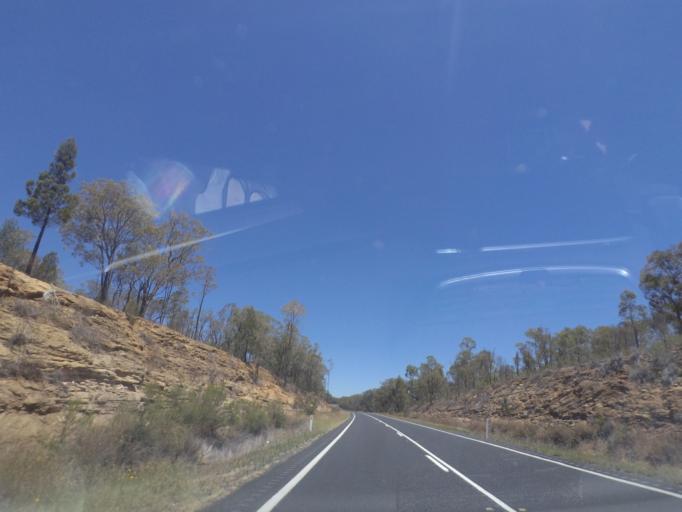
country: AU
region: New South Wales
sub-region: Warrumbungle Shire
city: Coonabarabran
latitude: -31.1811
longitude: 149.3555
